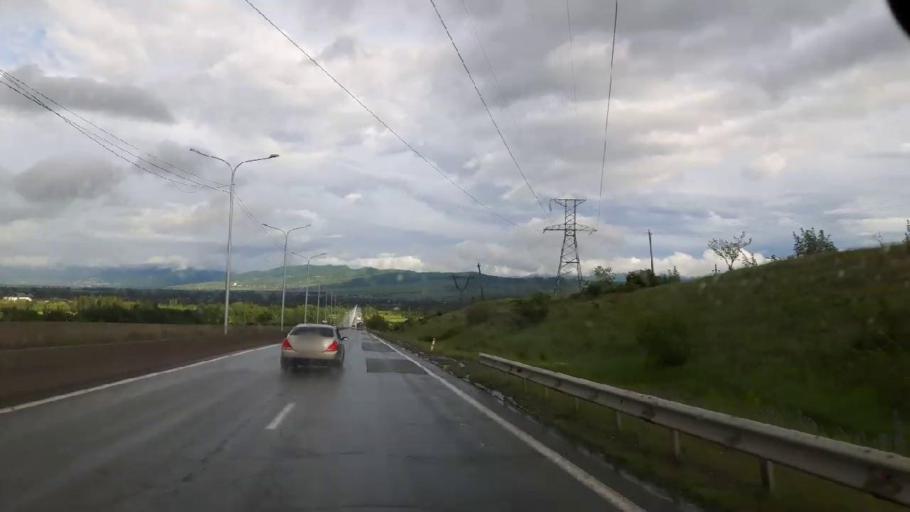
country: GE
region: Shida Kartli
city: Kaspi
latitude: 41.9285
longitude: 44.5308
